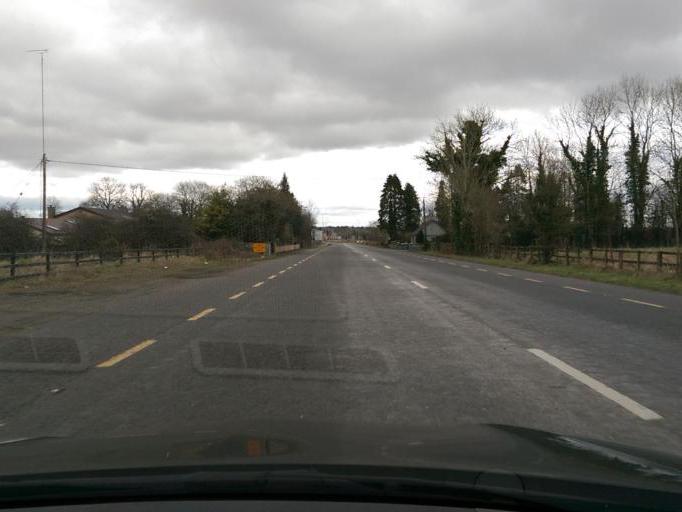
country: IE
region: Leinster
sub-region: An Iarmhi
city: Moate
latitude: 53.3957
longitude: -7.6945
